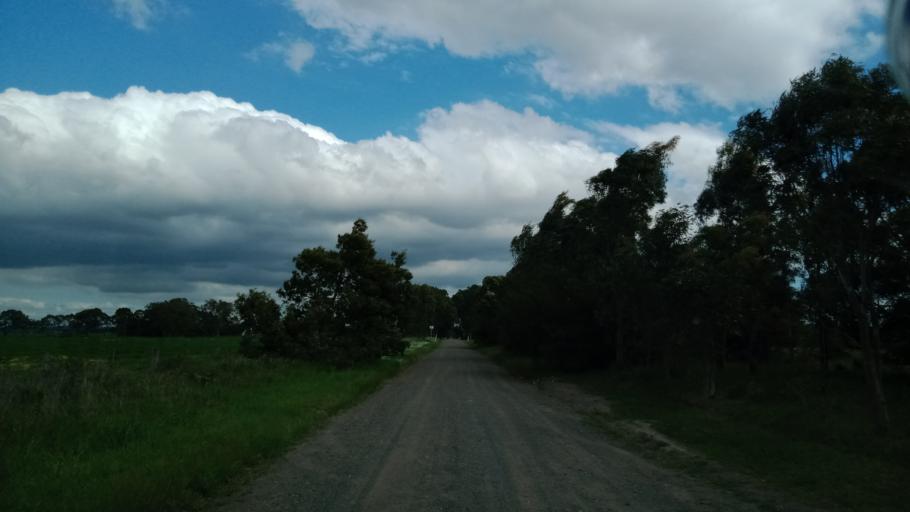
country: AU
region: Victoria
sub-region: Frankston
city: Sandhurst
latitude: -38.0869
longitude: 145.2191
